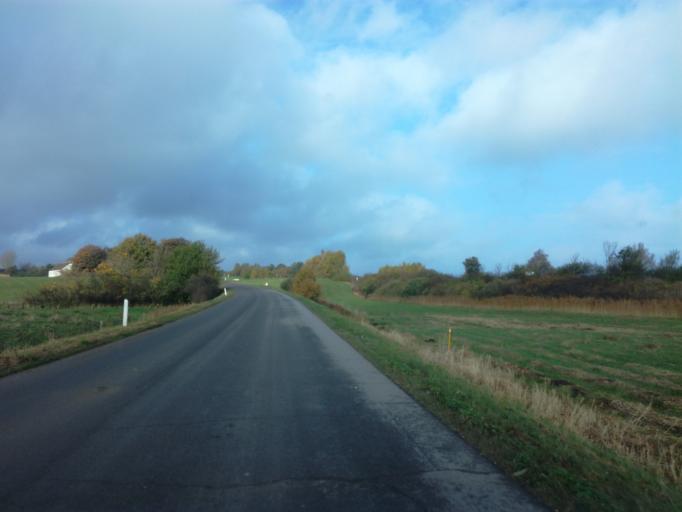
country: DK
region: South Denmark
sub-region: Fredericia Kommune
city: Fredericia
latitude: 55.6230
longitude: 9.7362
